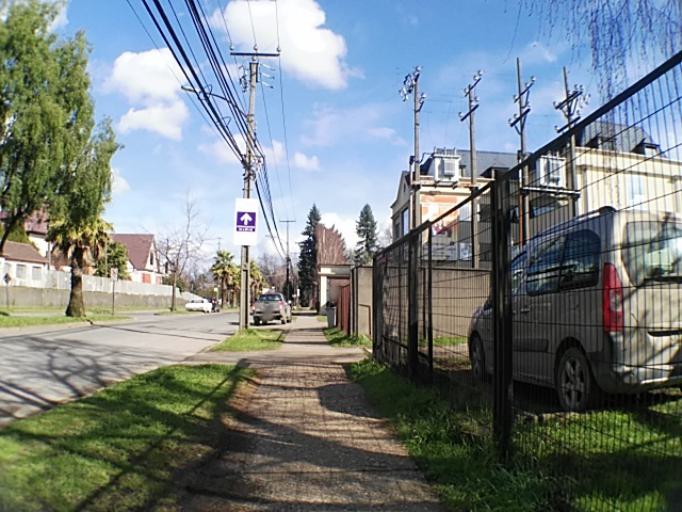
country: CL
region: Los Rios
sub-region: Provincia de Valdivia
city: Valdivia
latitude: -39.8301
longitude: -73.2410
